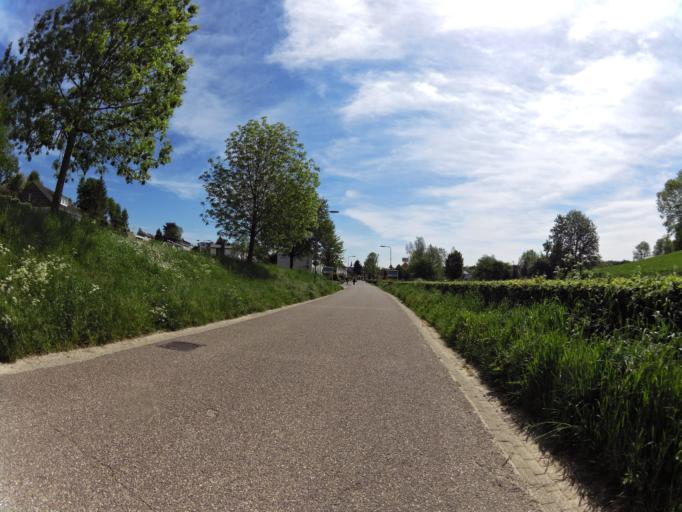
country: NL
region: Limburg
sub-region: Gemeente Simpelveld
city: Simpelveld
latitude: 50.8362
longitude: 5.9707
